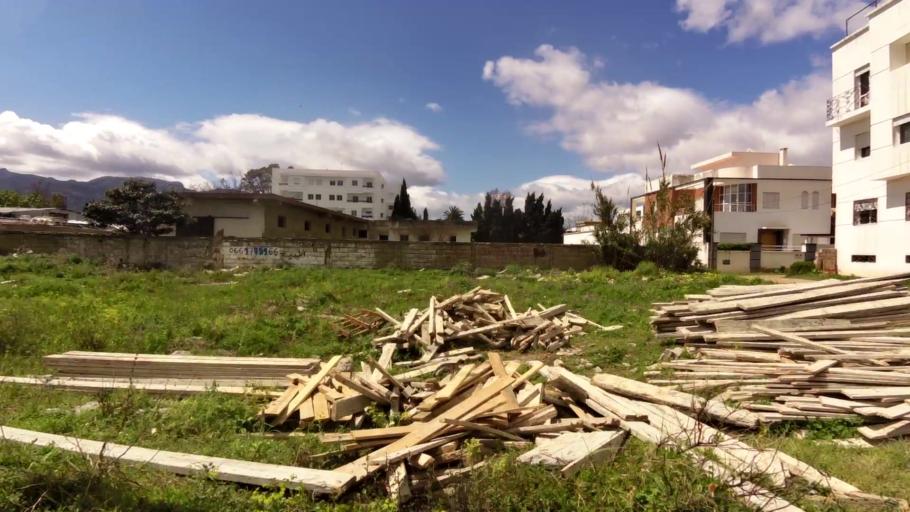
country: MA
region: Tanger-Tetouan
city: Tetouan
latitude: 35.5794
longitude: -5.3360
